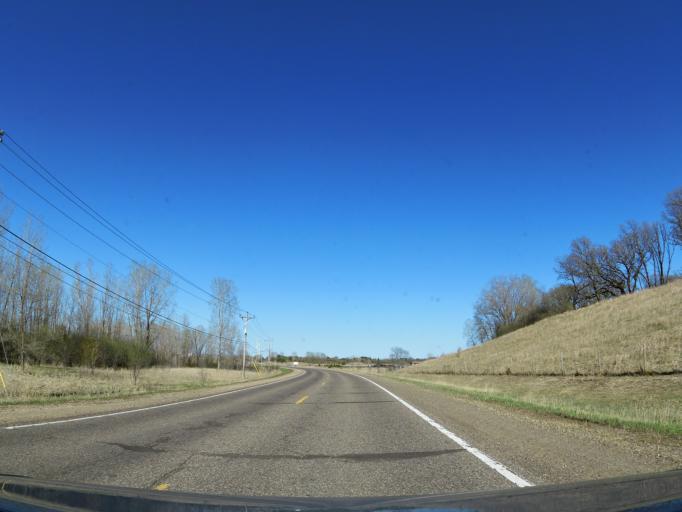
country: US
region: Minnesota
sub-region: Washington County
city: Lakeland
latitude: 44.9467
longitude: -92.8198
